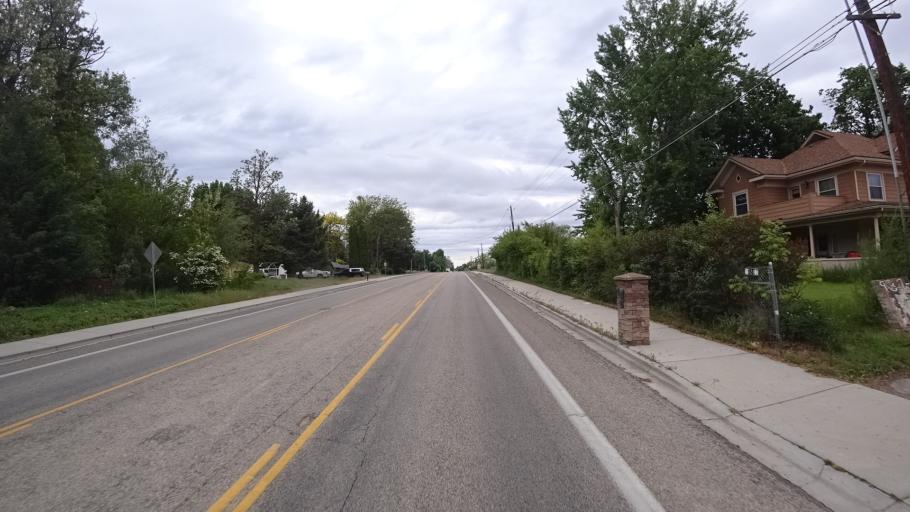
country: US
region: Idaho
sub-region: Ada County
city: Eagle
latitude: 43.7065
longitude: -116.3608
